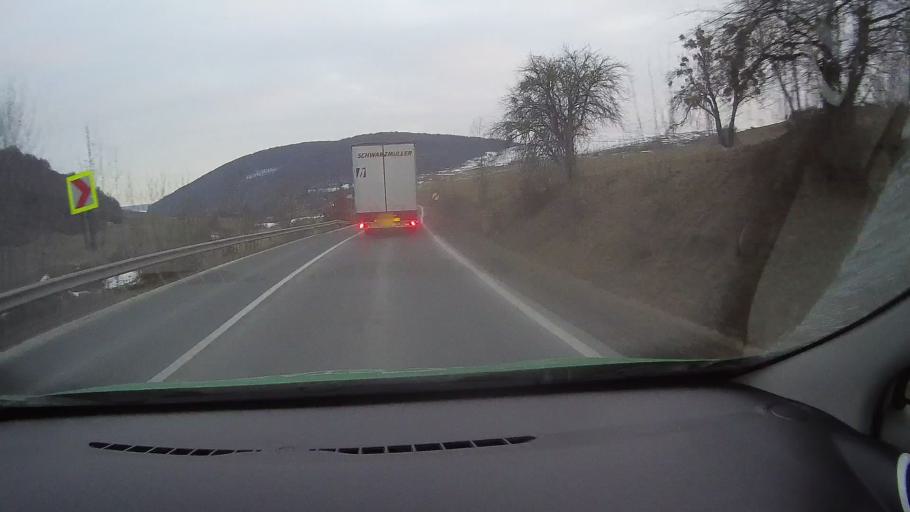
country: RO
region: Harghita
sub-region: Municipiul Odorheiu Secuiesc
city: Odorheiu Secuiesc
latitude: 46.3407
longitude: 25.2703
